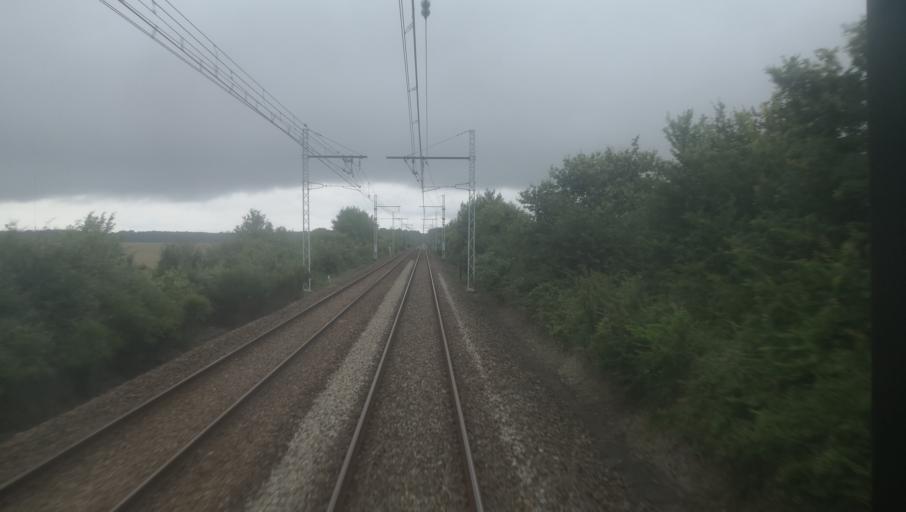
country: FR
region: Centre
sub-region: Departement de l'Indre
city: Luant
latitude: 46.7033
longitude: 1.5689
